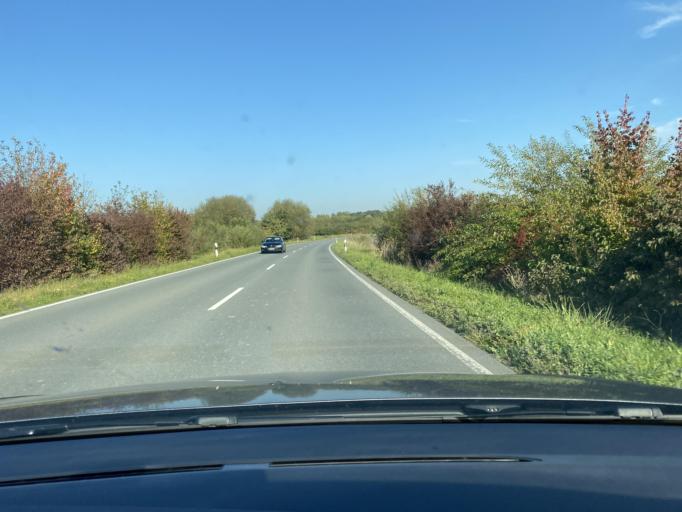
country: DE
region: North Rhine-Westphalia
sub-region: Regierungsbezirk Munster
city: Billerbeck
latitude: 52.0280
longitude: 7.2584
